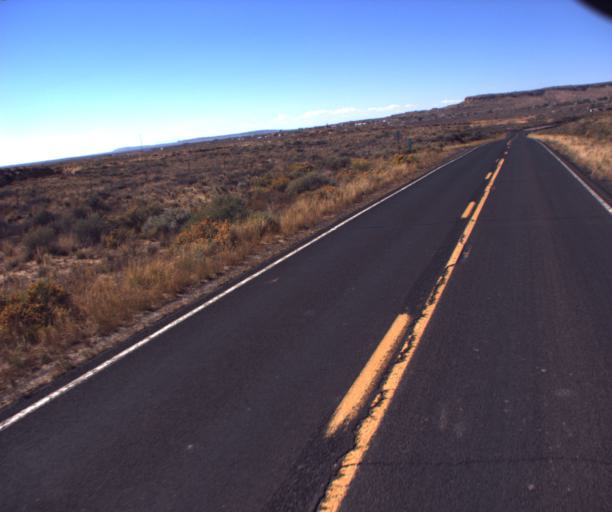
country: US
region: Arizona
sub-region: Navajo County
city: First Mesa
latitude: 35.8732
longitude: -110.5958
